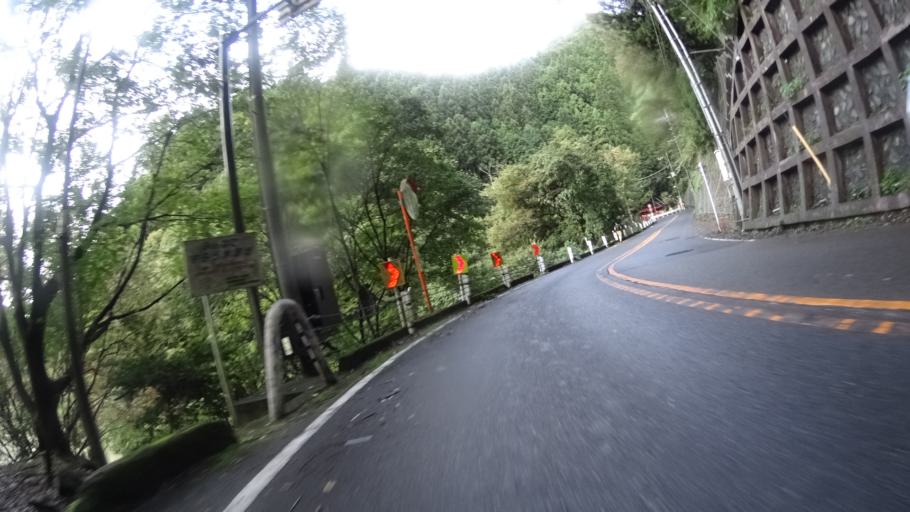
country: JP
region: Yamanashi
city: Uenohara
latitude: 35.7841
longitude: 139.0318
